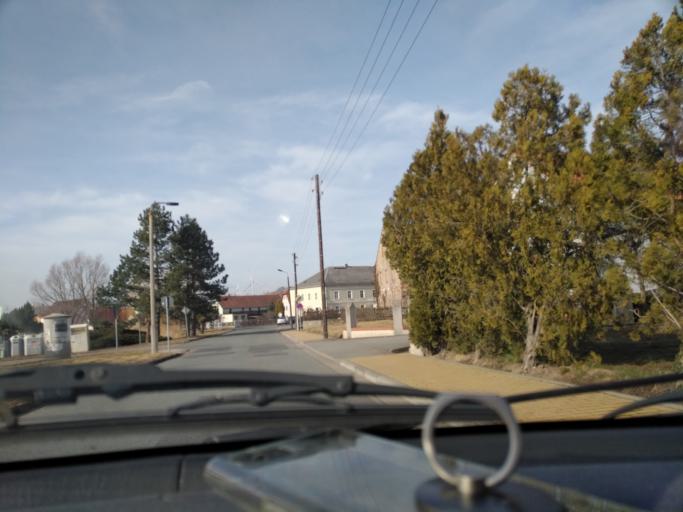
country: DE
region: Saxony
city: Glaubitz
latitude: 51.3239
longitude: 13.3801
